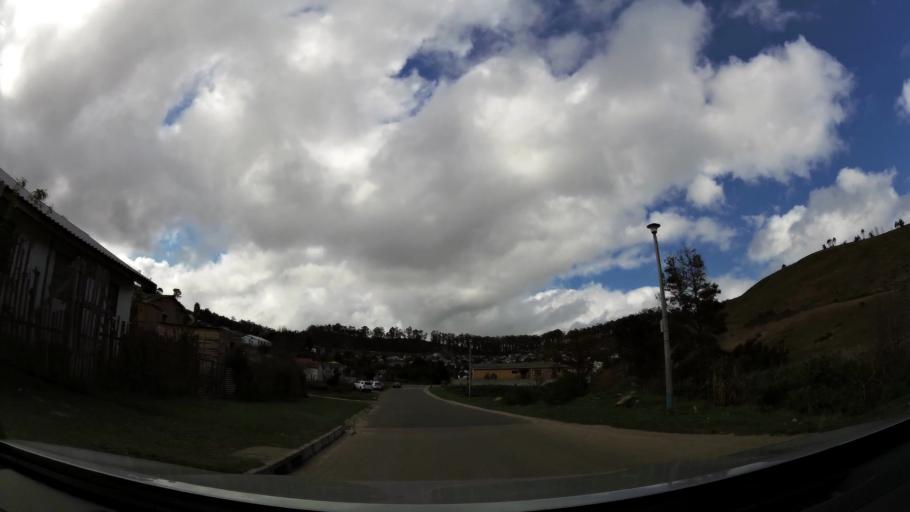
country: ZA
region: Western Cape
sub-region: Eden District Municipality
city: Knysna
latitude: -34.0537
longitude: 23.0983
